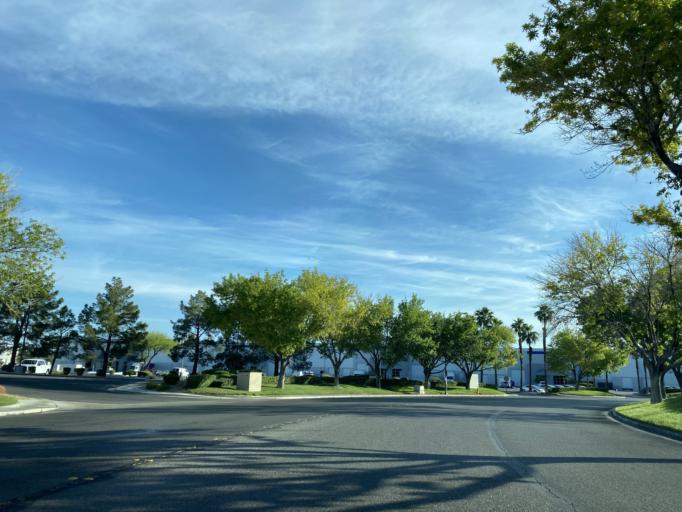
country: US
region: Nevada
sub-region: Clark County
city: Paradise
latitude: 36.0655
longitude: -115.1428
